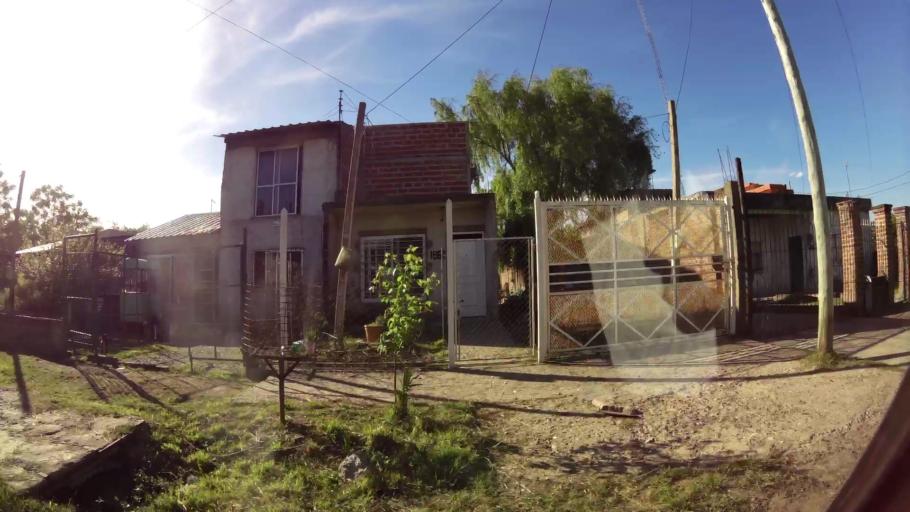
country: AR
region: Buenos Aires
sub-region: Partido de Almirante Brown
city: Adrogue
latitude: -34.8269
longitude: -58.3570
